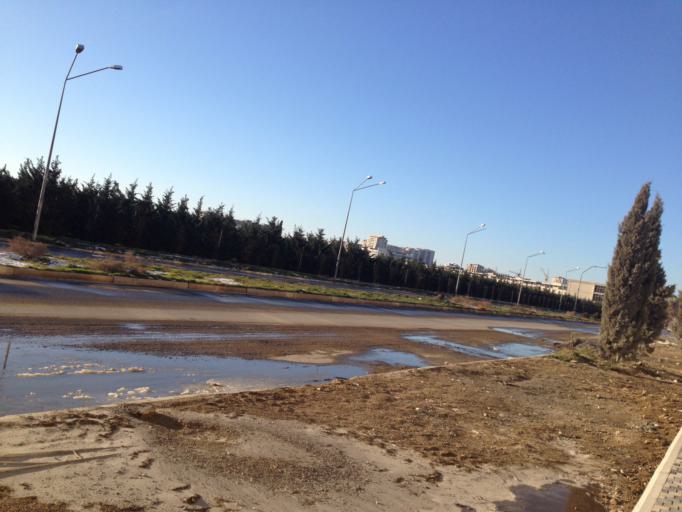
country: AZ
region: Baki
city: Baku
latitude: 40.4080
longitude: 49.8601
